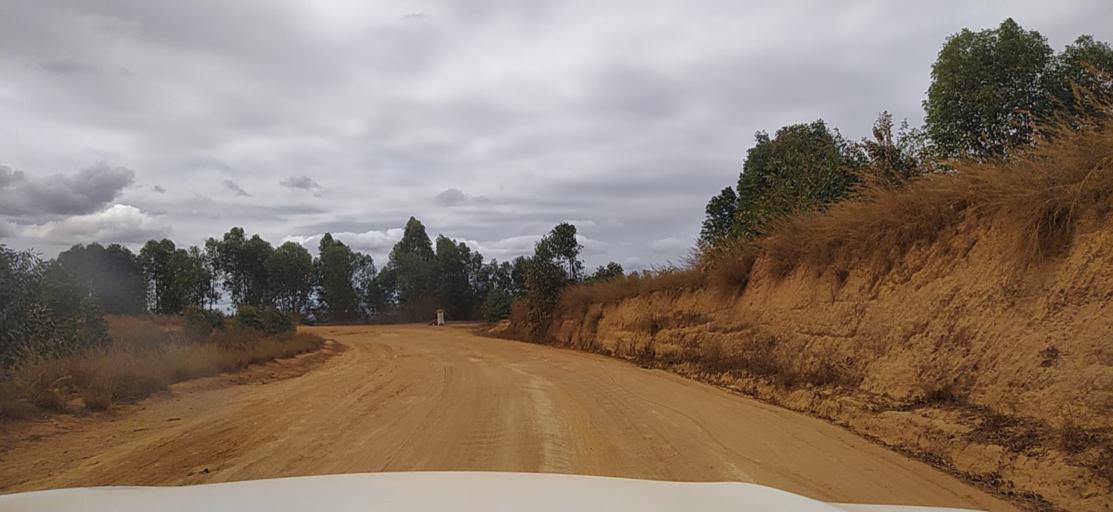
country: MG
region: Alaotra Mangoro
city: Ambatondrazaka
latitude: -17.9974
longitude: 48.2675
